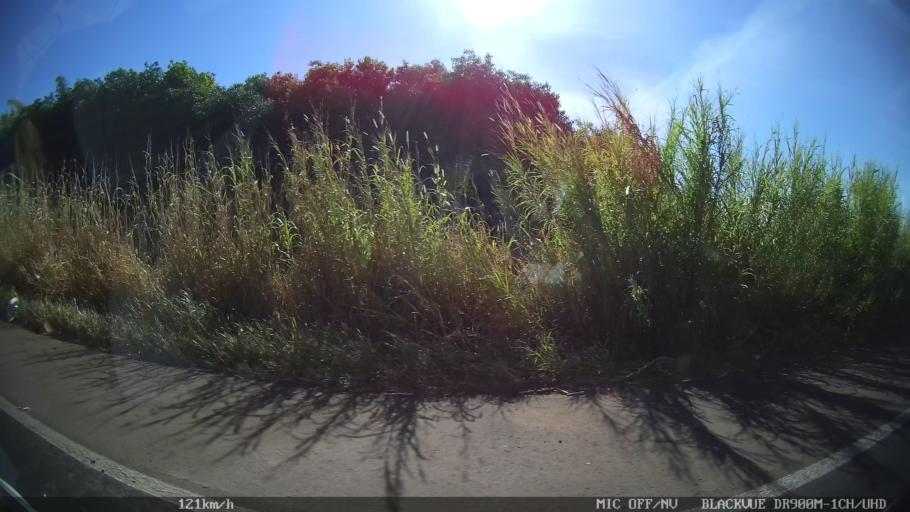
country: BR
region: Sao Paulo
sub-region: Olimpia
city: Olimpia
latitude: -20.6388
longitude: -48.8243
